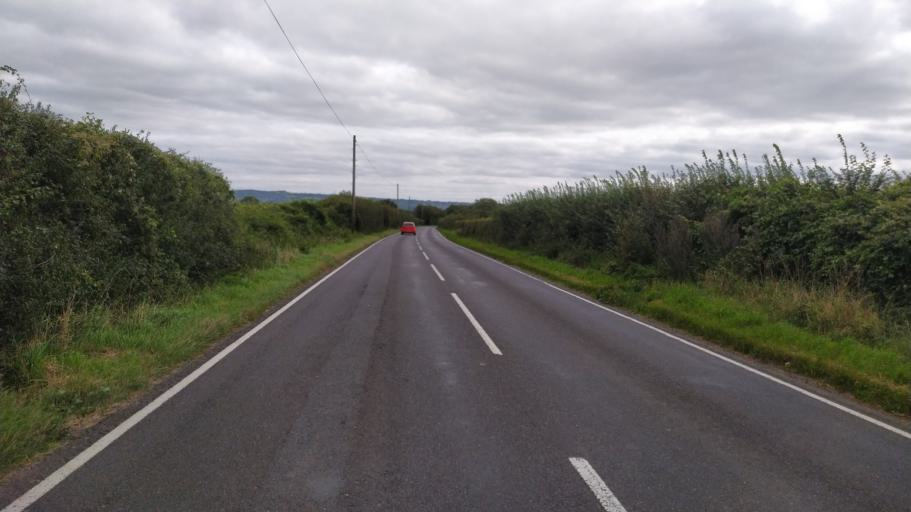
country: GB
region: England
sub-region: Dorset
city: Gillingham
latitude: 51.0456
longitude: -2.3137
